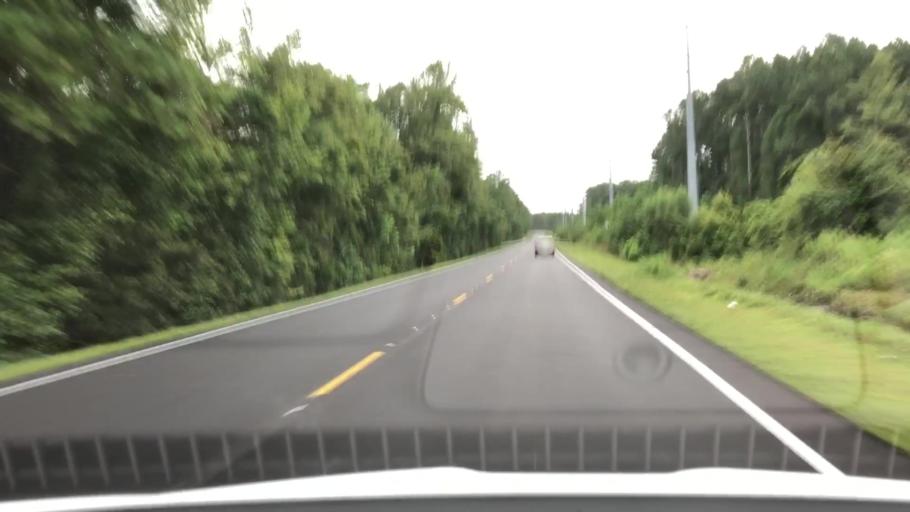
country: US
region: North Carolina
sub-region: Carteret County
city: Cape Carteret
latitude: 34.7636
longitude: -77.0956
